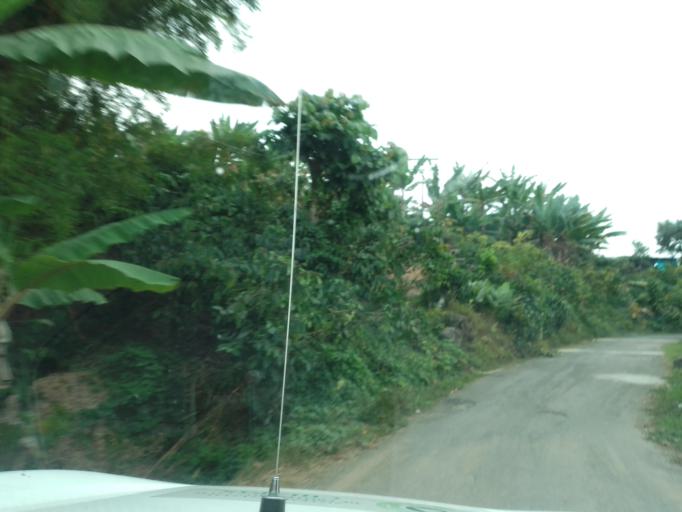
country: MX
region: Chiapas
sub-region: Union Juarez
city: Santo Domingo
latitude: 15.0541
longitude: -92.1247
